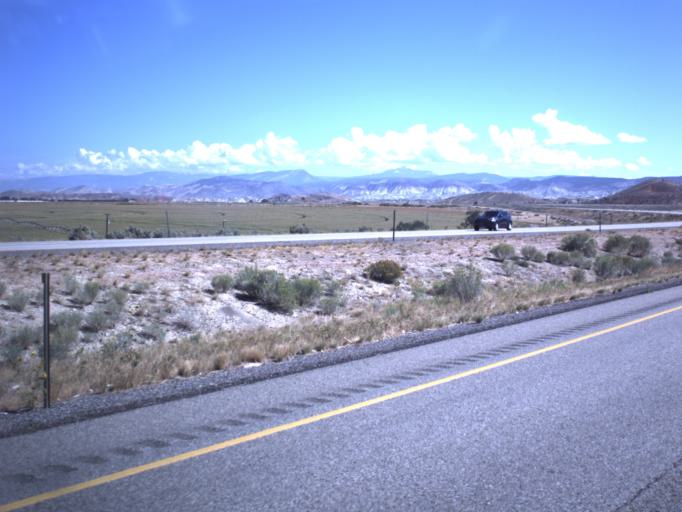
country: US
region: Utah
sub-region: Sevier County
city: Aurora
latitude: 38.8784
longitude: -111.9350
